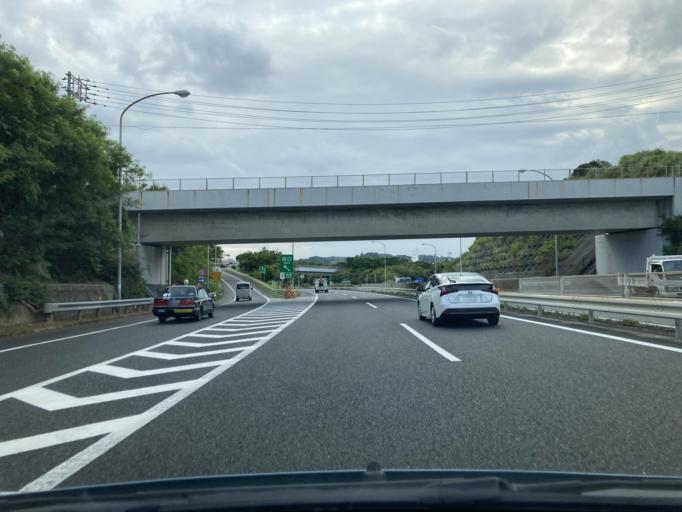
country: JP
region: Okinawa
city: Ginowan
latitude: 26.2486
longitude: 127.7527
